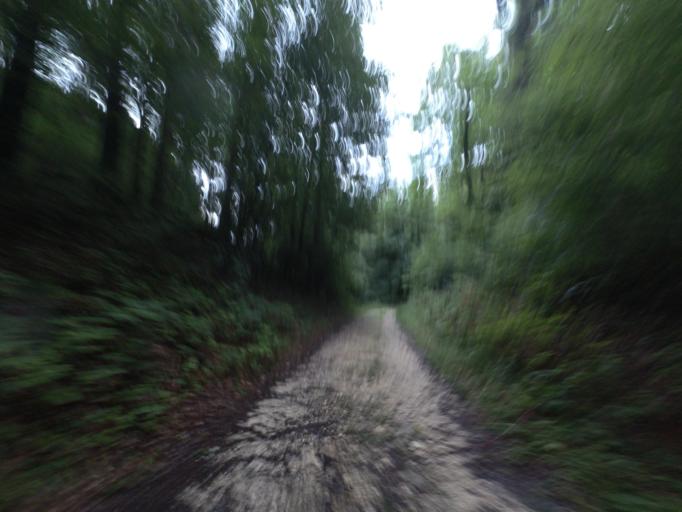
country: AT
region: Salzburg
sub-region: Politischer Bezirk Salzburg-Umgebung
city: Grodig
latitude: 47.7384
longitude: 13.0303
